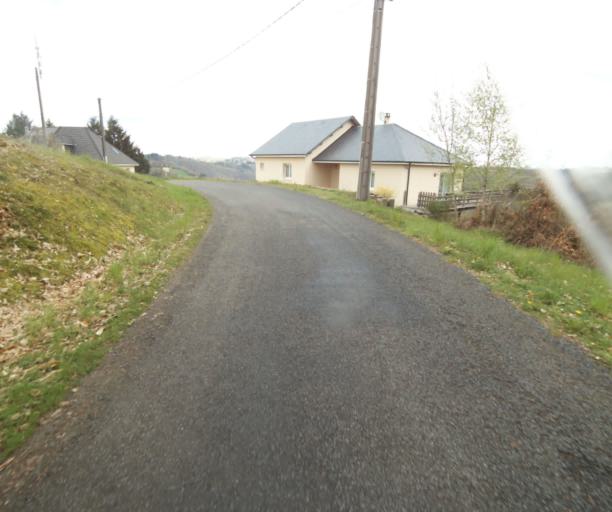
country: FR
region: Limousin
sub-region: Departement de la Correze
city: Naves
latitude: 45.2964
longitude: 1.8060
